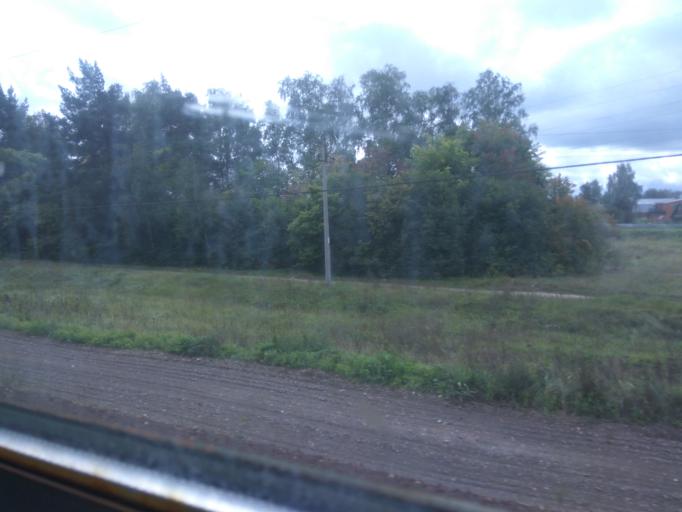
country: RU
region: Moskovskaya
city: Beloozerskiy
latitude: 55.4825
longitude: 38.4022
